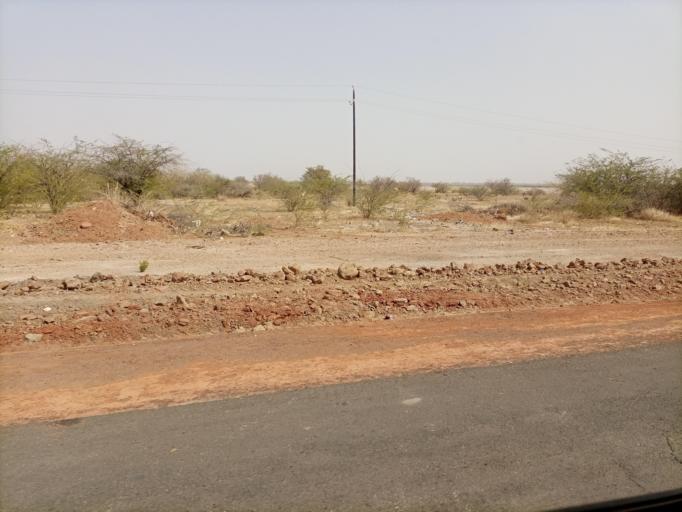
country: SN
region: Fatick
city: Foundiougne
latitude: 14.1574
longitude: -16.4688
